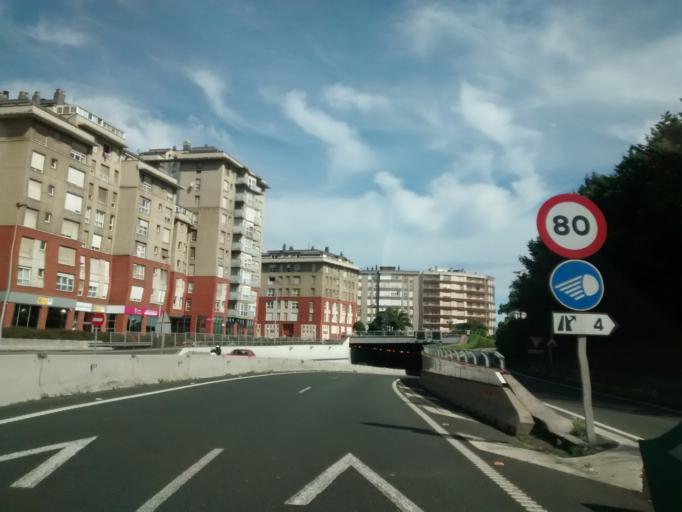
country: ES
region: Cantabria
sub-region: Provincia de Cantabria
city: El Astillero
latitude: 43.4167
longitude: -3.8397
